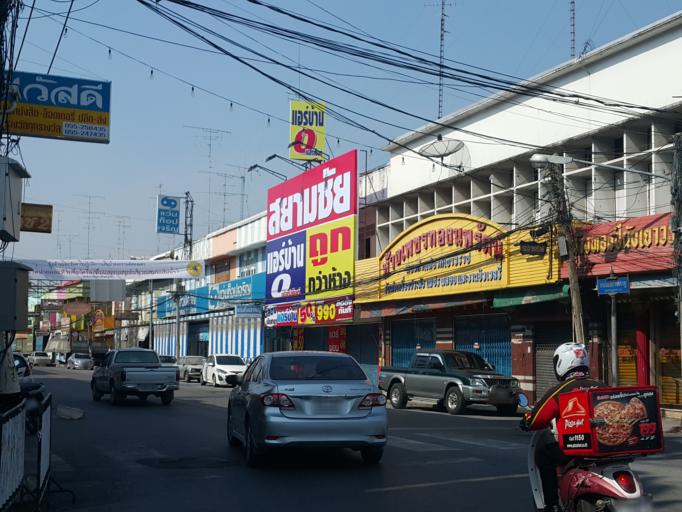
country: TH
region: Phitsanulok
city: Phitsanulok
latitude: 16.8150
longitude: 100.2647
